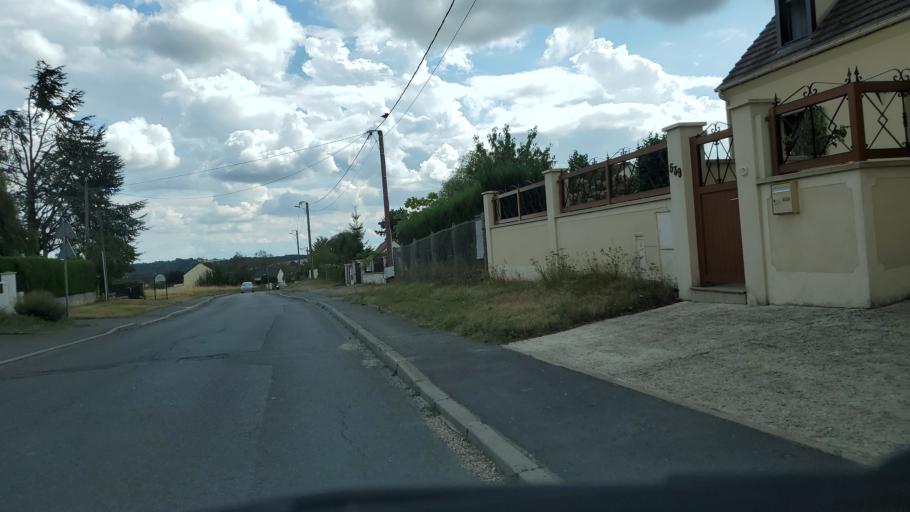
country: FR
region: Ile-de-France
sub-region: Departement de Seine-et-Marne
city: Mouroux
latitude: 48.8300
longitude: 3.0352
